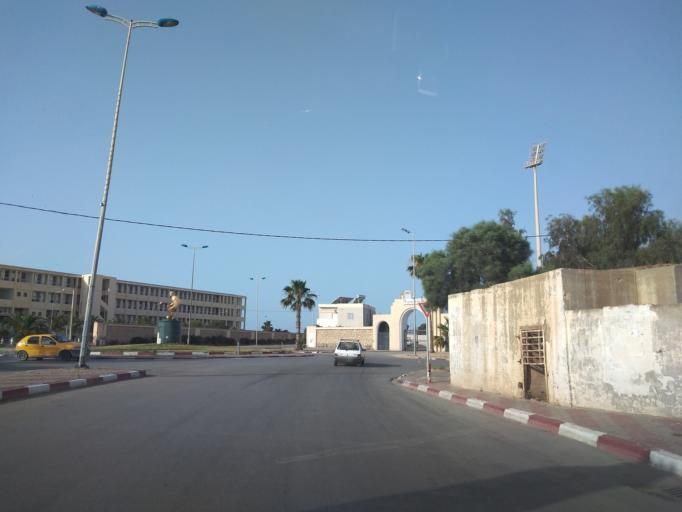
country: TN
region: Safaqis
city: Sfax
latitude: 34.7346
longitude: 10.7483
